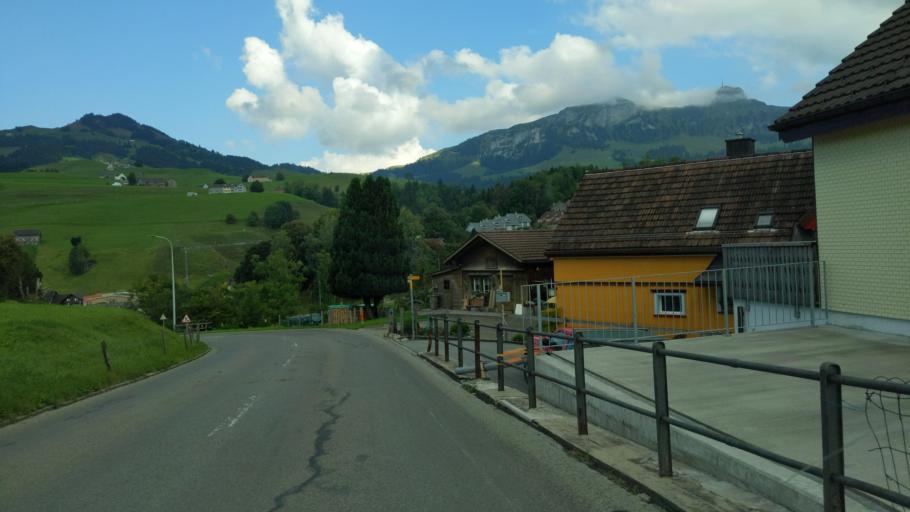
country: CH
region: Appenzell Innerrhoden
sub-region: Appenzell Inner Rhodes
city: Appenzell
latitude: 47.3071
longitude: 9.4332
